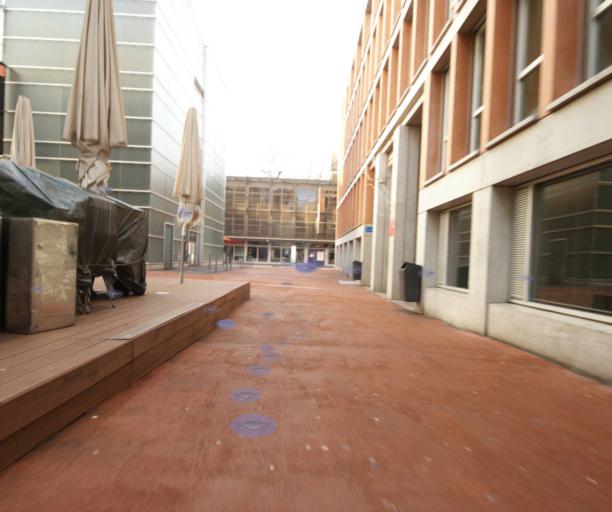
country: CH
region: Vaud
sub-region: Lausanne District
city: Lausanne
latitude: 46.5220
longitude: 6.6262
